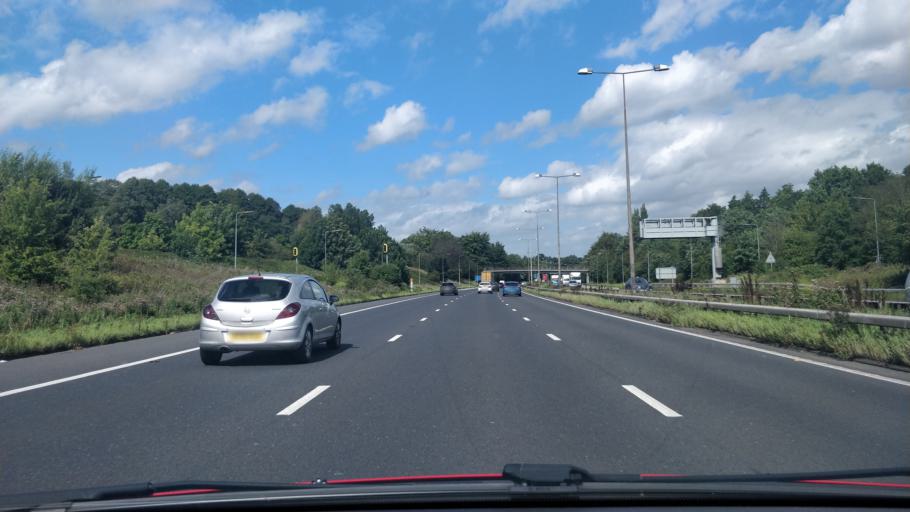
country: GB
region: England
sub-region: Borough of Wigan
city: Ashton in Makerfield
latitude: 53.4879
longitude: -2.6538
